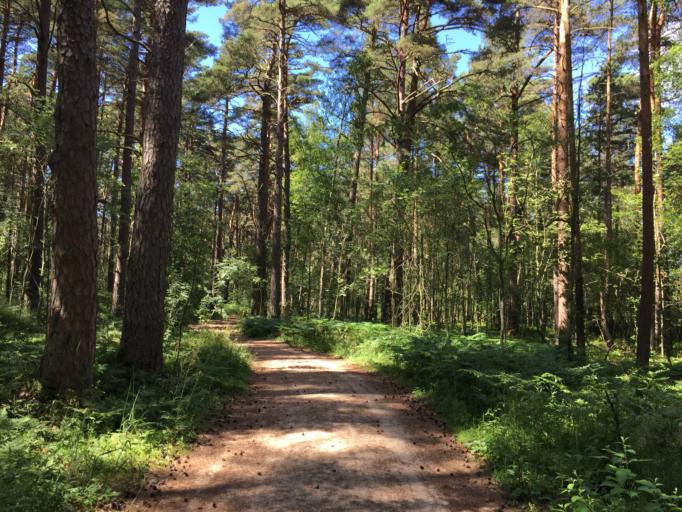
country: LV
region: Ventspils
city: Ventspils
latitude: 57.4466
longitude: 21.6309
